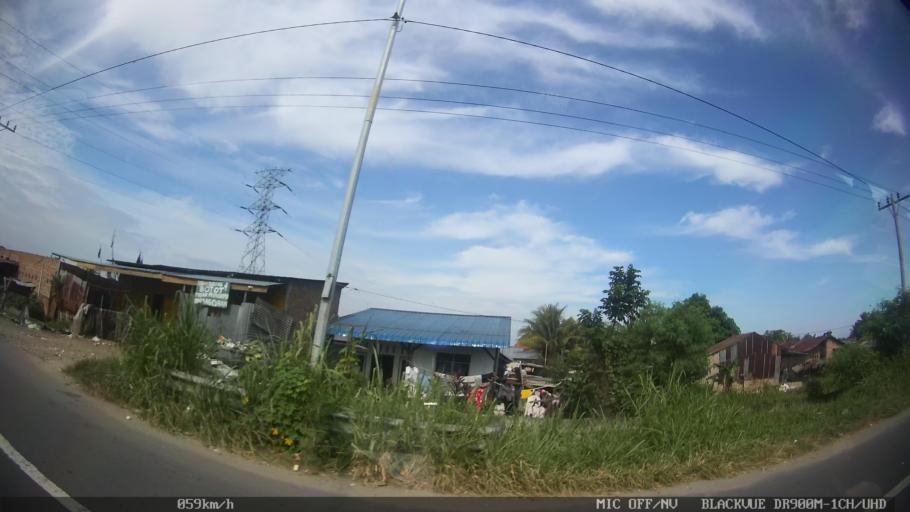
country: ID
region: North Sumatra
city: Sunggal
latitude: 3.6177
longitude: 98.6285
